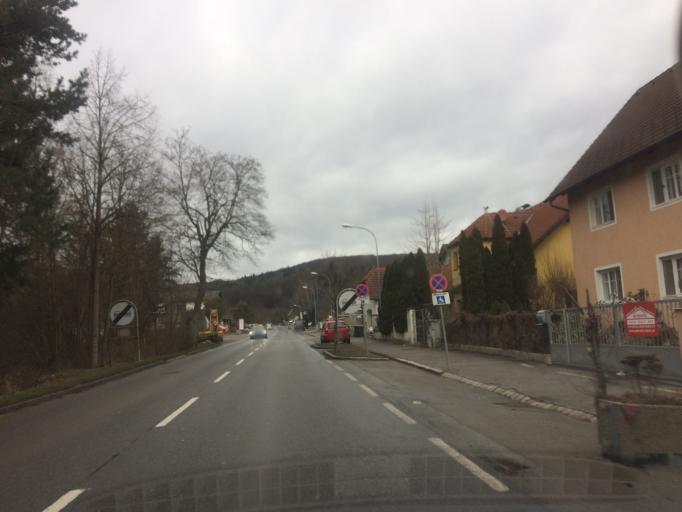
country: AT
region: Lower Austria
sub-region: Politischer Bezirk Wien-Umgebung
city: Gablitz
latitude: 48.2381
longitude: 16.1383
